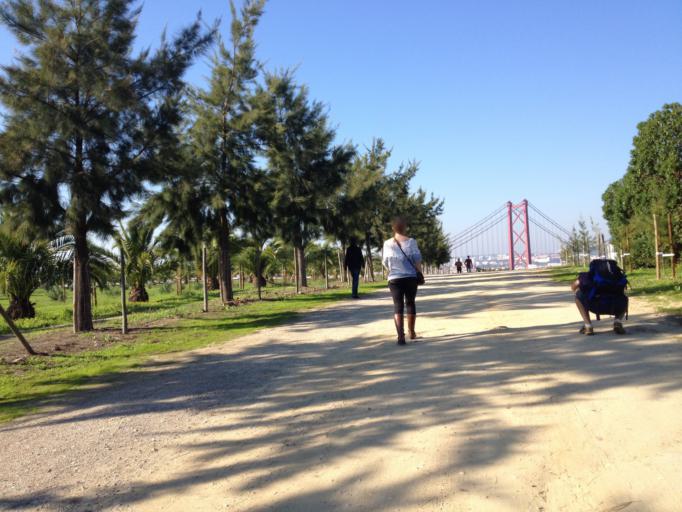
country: PT
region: Setubal
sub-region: Almada
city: Pragal
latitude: 38.6788
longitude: -9.1694
